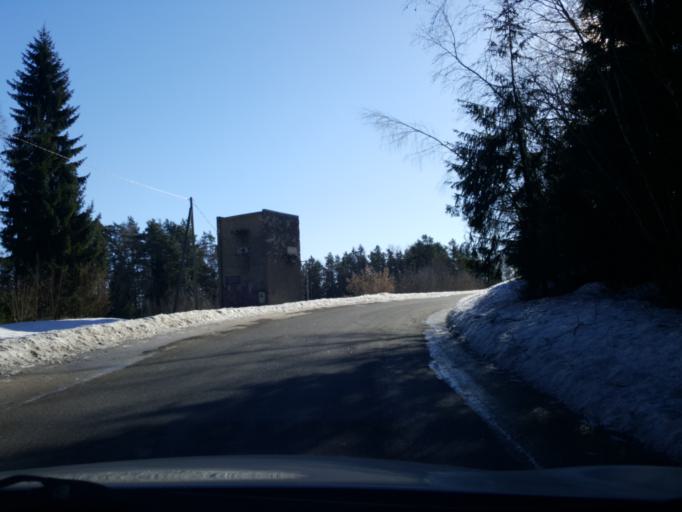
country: EE
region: Viljandimaa
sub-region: Viiratsi vald
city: Viiratsi
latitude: 58.4343
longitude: 25.6837
